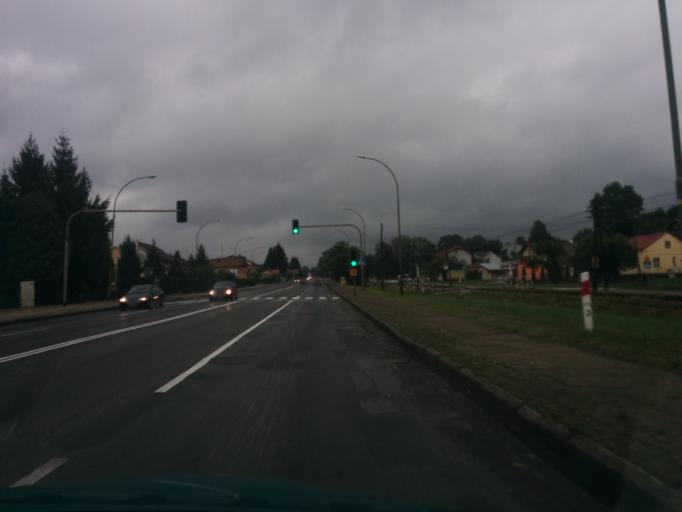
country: PL
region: Subcarpathian Voivodeship
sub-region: Powiat sanocki
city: Sanok
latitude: 49.5686
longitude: 22.1666
